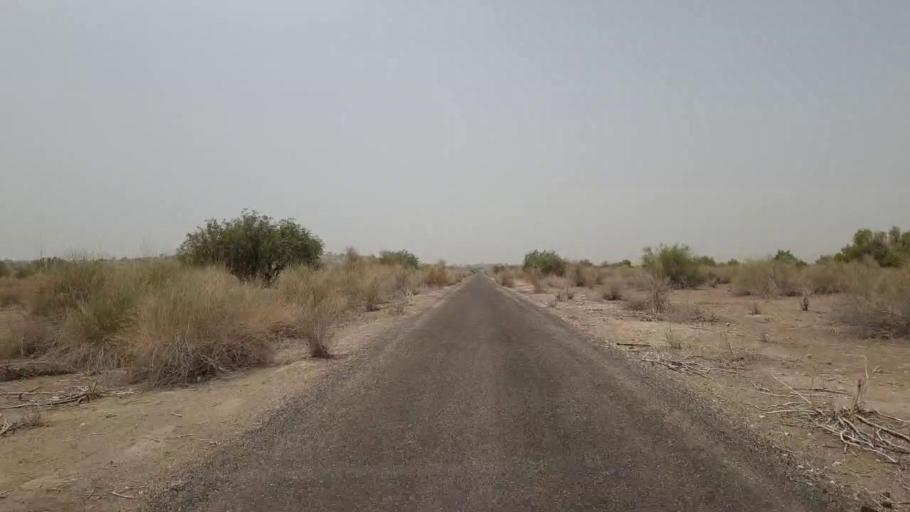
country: PK
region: Sindh
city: Islamkot
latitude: 24.7741
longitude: 70.4919
